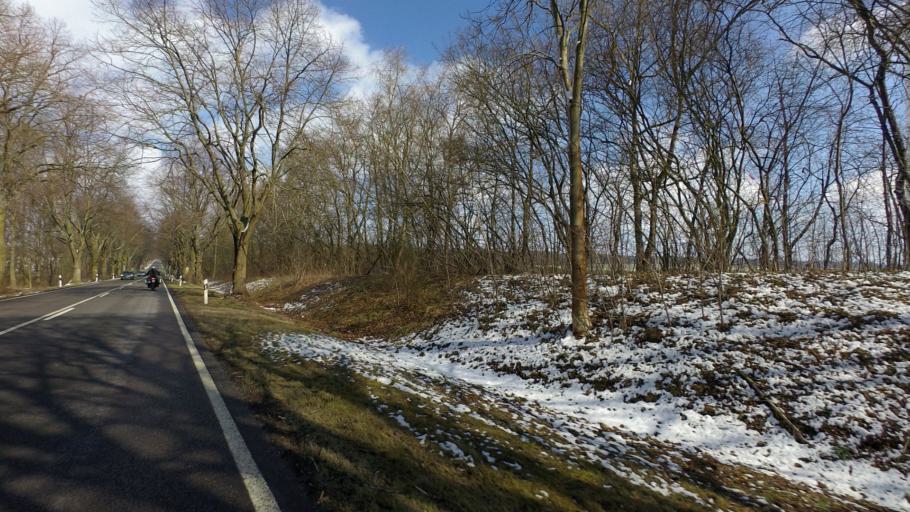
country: DE
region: Brandenburg
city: Werftpfuhl
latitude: 52.7037
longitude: 13.8368
